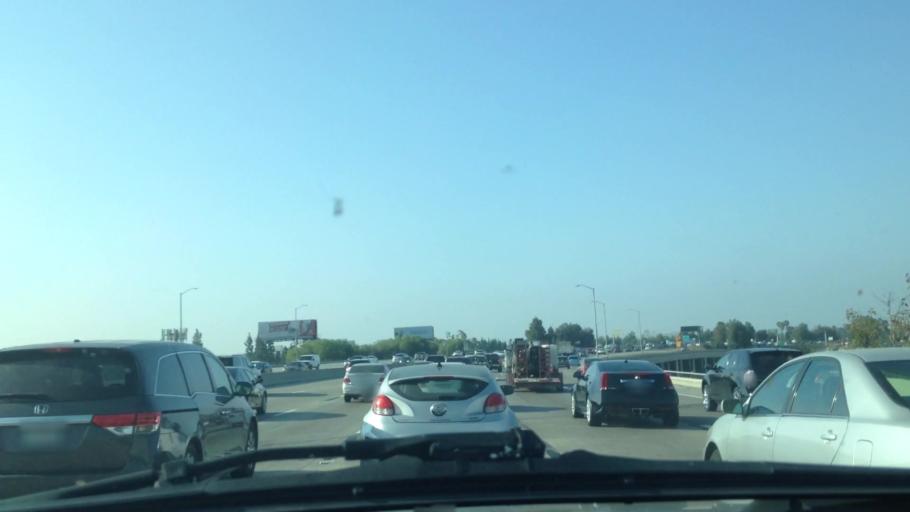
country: US
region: California
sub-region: Orange County
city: Orange
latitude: 33.8003
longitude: -117.8783
